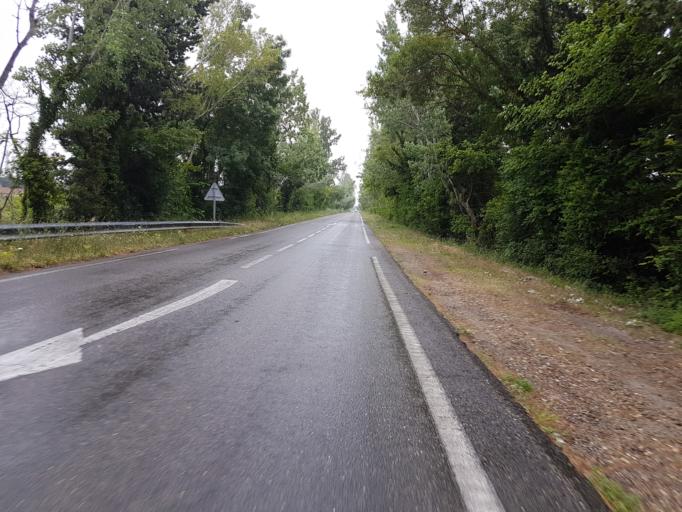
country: FR
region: Languedoc-Roussillon
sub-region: Departement du Gard
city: Villeneuve-les-Avignon
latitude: 43.9937
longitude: 4.8232
